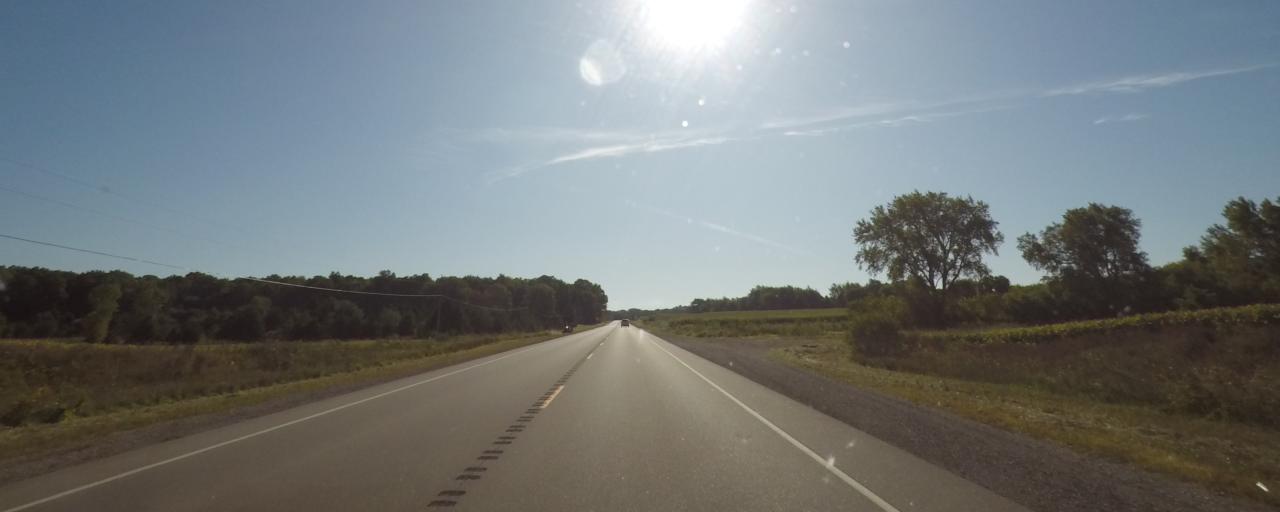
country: US
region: Wisconsin
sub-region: Jefferson County
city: Lake Ripley
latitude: 43.0107
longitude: -88.9598
